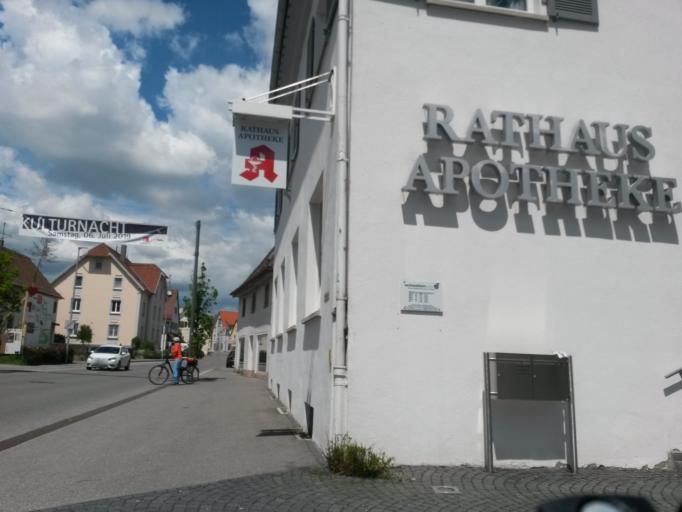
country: DE
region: Baden-Wuerttemberg
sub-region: Tuebingen Region
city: Bad Schussenried
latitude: 48.0067
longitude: 9.6556
